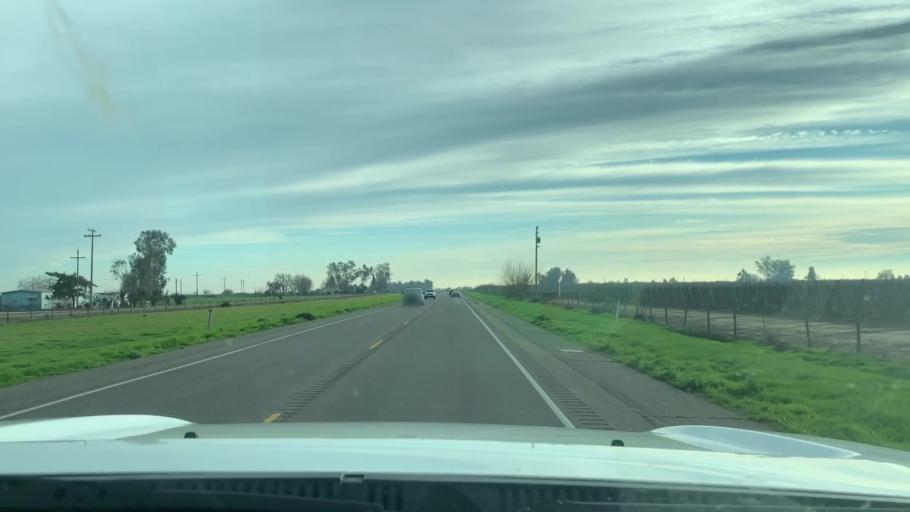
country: US
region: California
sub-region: Fresno County
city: Caruthers
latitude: 36.4757
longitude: -119.7932
